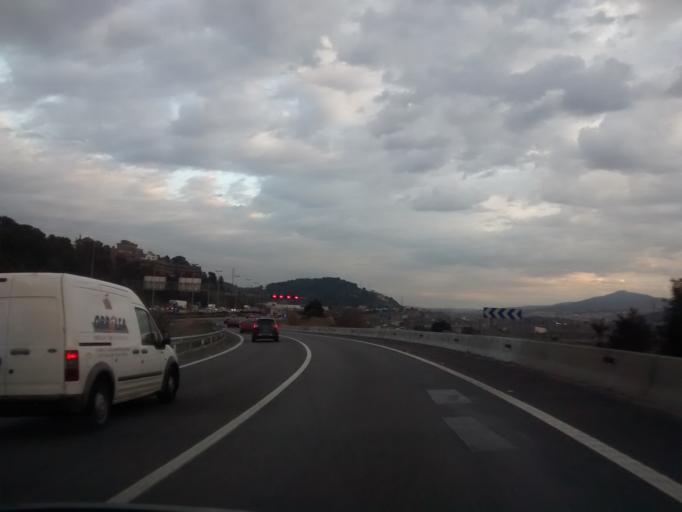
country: ES
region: Catalonia
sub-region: Provincia de Barcelona
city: Palleja
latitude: 41.4407
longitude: 1.9993
